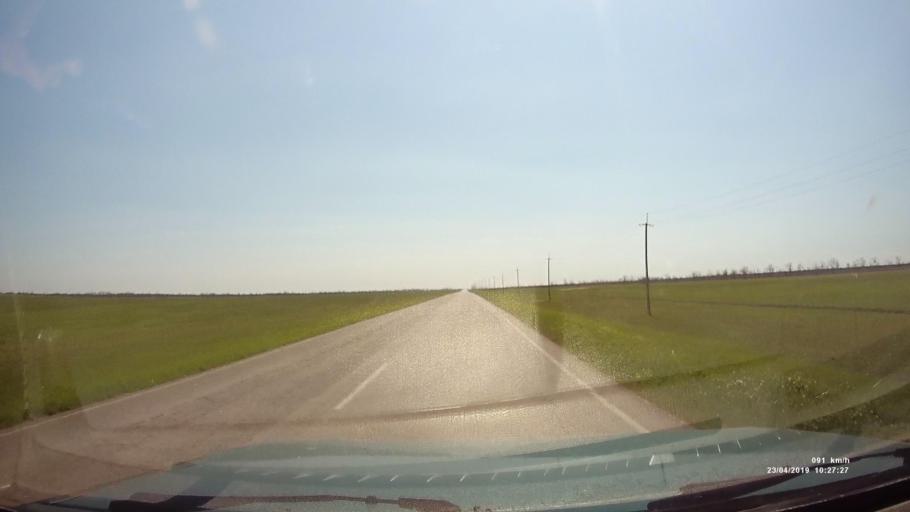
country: RU
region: Kalmykiya
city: Yashalta
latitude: 46.6133
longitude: 42.4919
